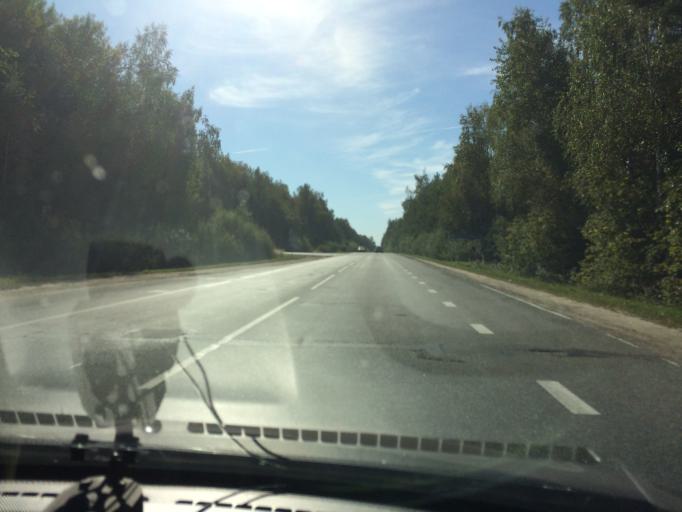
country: RU
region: Mariy-El
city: Yoshkar-Ola
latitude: 56.5686
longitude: 47.9731
